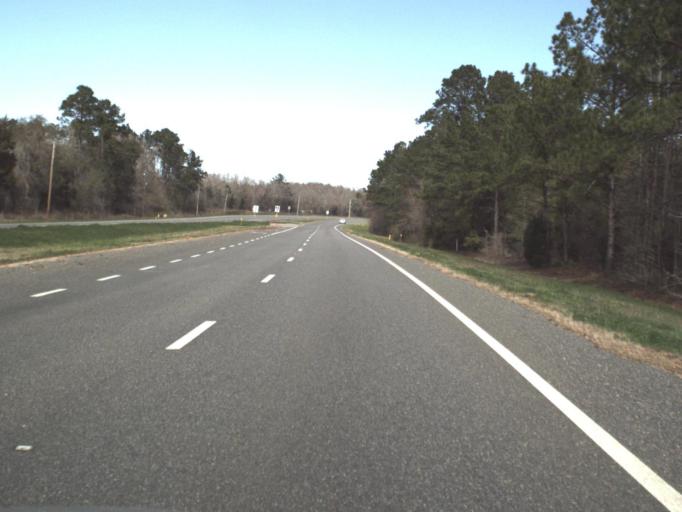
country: US
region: Florida
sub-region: Washington County
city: Chipley
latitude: 30.7417
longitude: -85.3852
